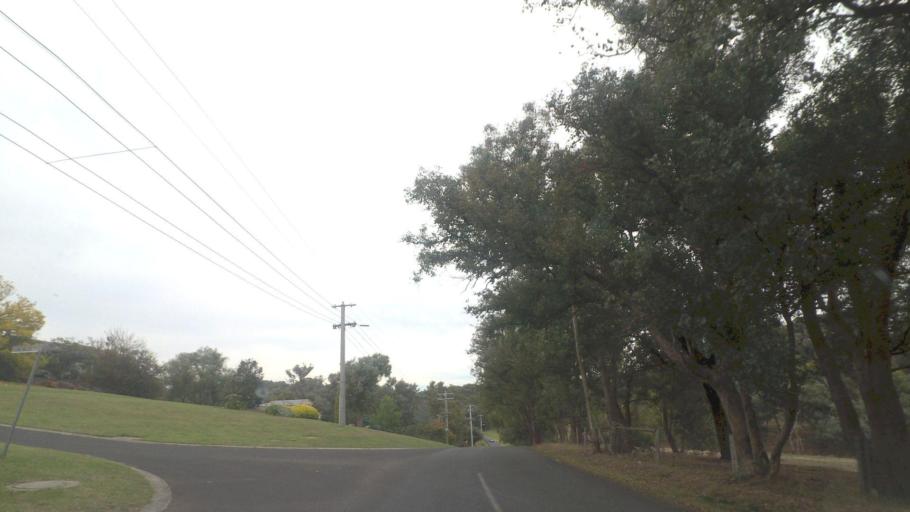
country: AU
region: Victoria
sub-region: Nillumbik
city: North Warrandyte
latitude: -37.7413
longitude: 145.1848
